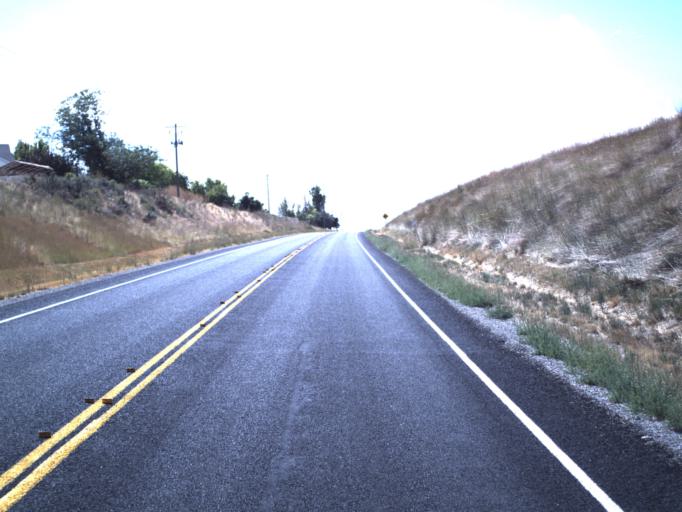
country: US
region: Utah
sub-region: Box Elder County
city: Garland
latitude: 41.8317
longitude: -112.1460
